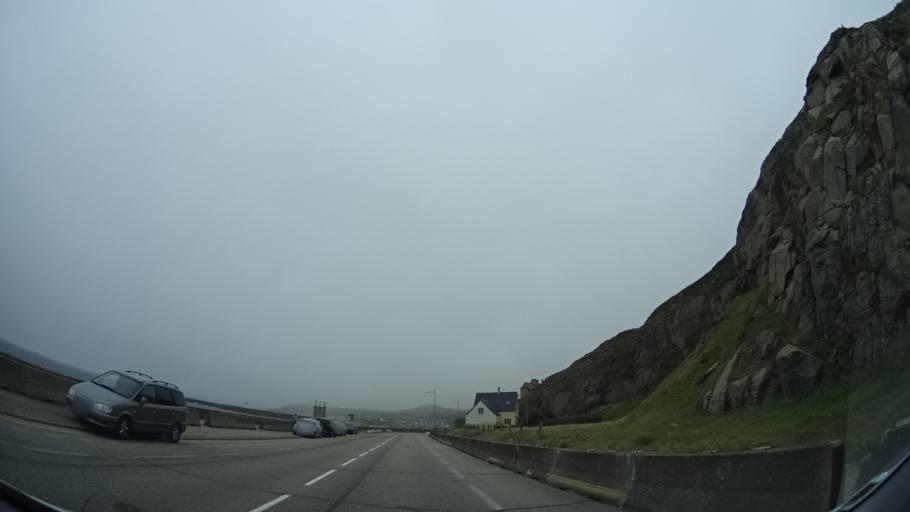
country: FR
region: Lower Normandy
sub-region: Departement de la Manche
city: Flamanville
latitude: 49.5482
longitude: -1.8686
